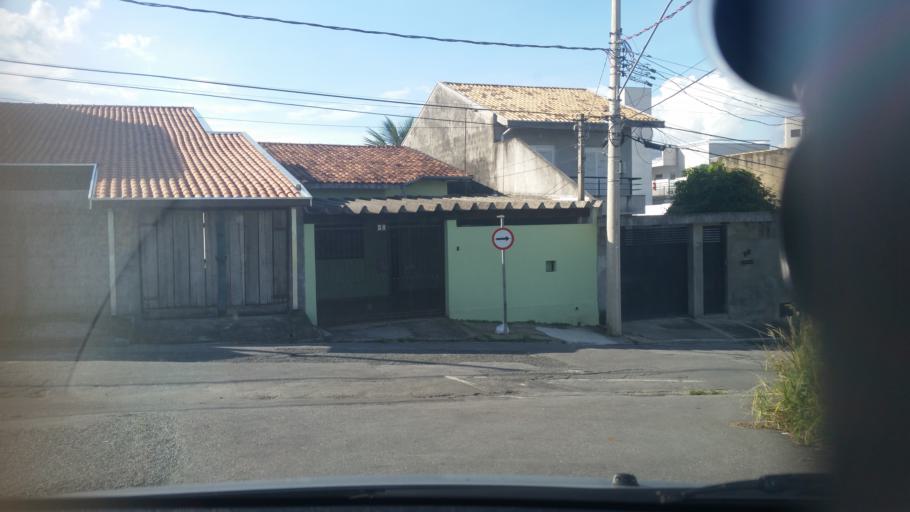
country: BR
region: Sao Paulo
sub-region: Taubate
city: Taubate
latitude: -23.0271
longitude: -45.5732
